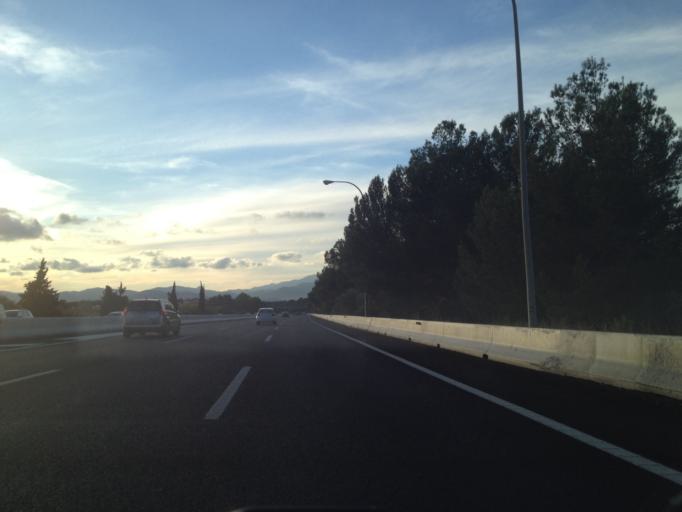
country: ES
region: Balearic Islands
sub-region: Illes Balears
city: Marratxi
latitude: 39.6300
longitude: 2.7329
